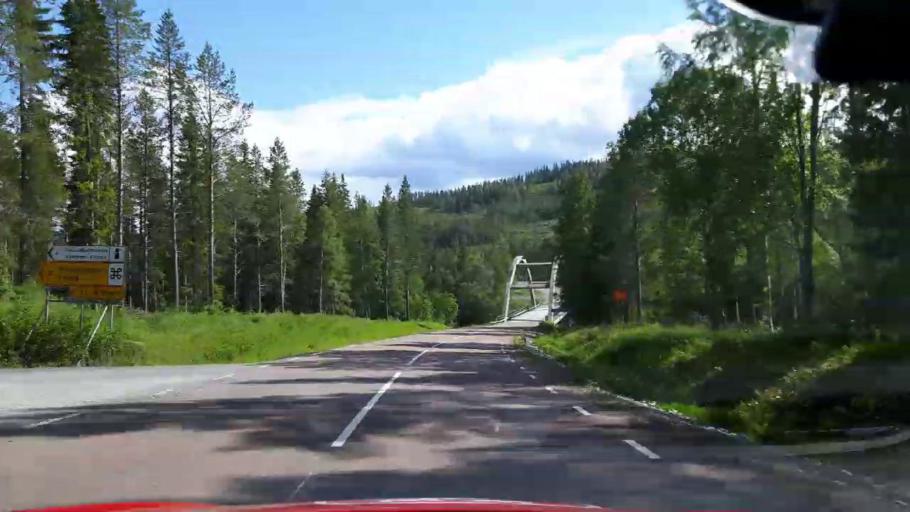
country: SE
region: Jaemtland
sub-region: Krokoms Kommun
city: Valla
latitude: 64.0198
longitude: 14.2074
